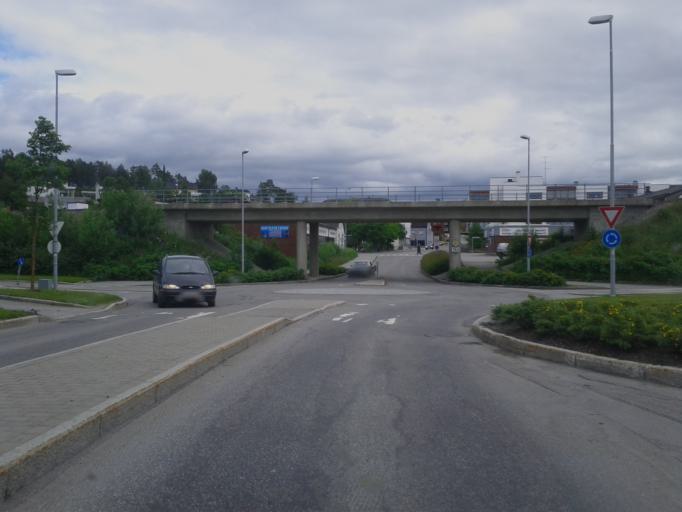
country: NO
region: Nord-Trondelag
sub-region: Steinkjer
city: Steinkjer
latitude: 64.0188
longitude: 11.4918
